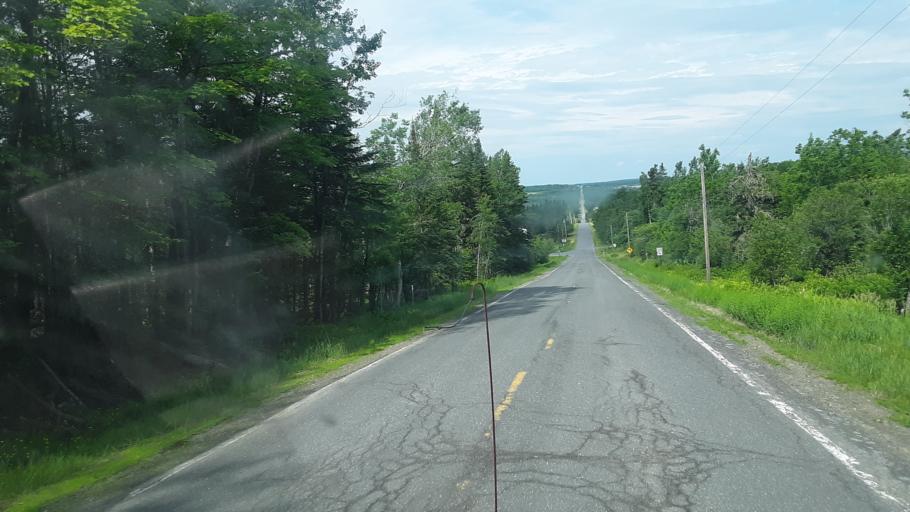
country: US
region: Maine
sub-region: Aroostook County
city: Caribou
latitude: 46.8786
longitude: -68.2171
